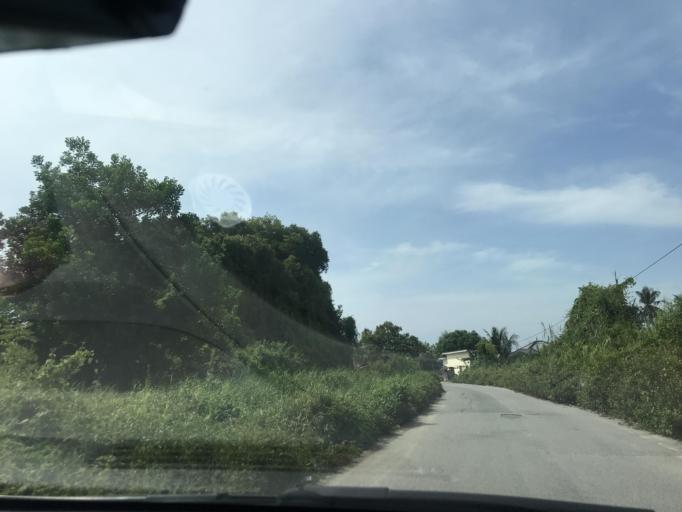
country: MY
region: Kelantan
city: Tumpat
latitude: 6.2217
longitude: 102.1184
